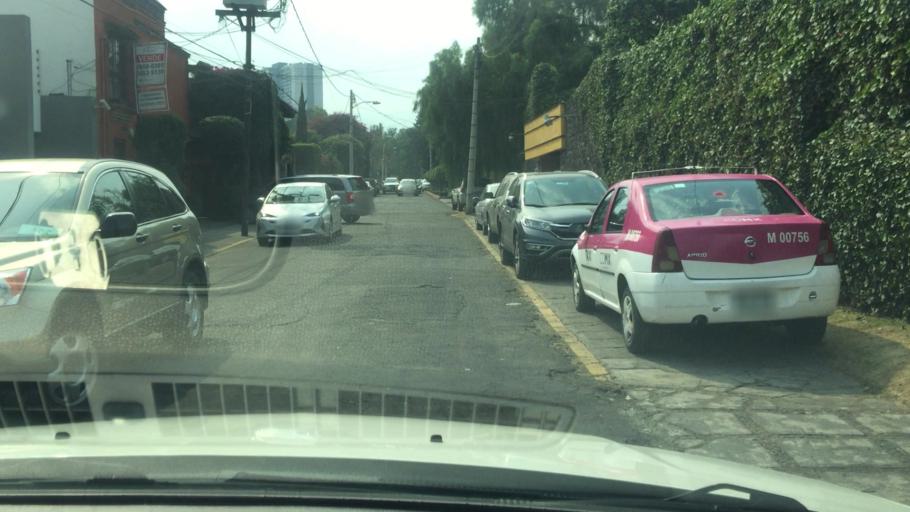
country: MX
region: Mexico City
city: Magdalena Contreras
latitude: 19.3141
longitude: -99.2097
